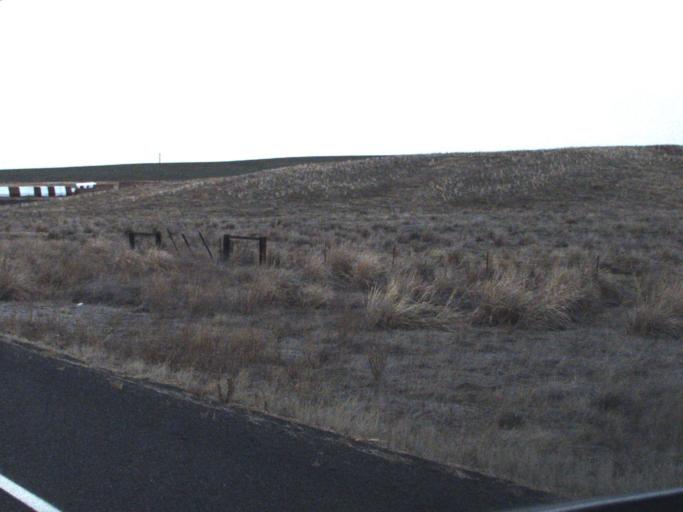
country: US
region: Washington
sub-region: Garfield County
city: Pomeroy
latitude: 46.7850
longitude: -117.9301
